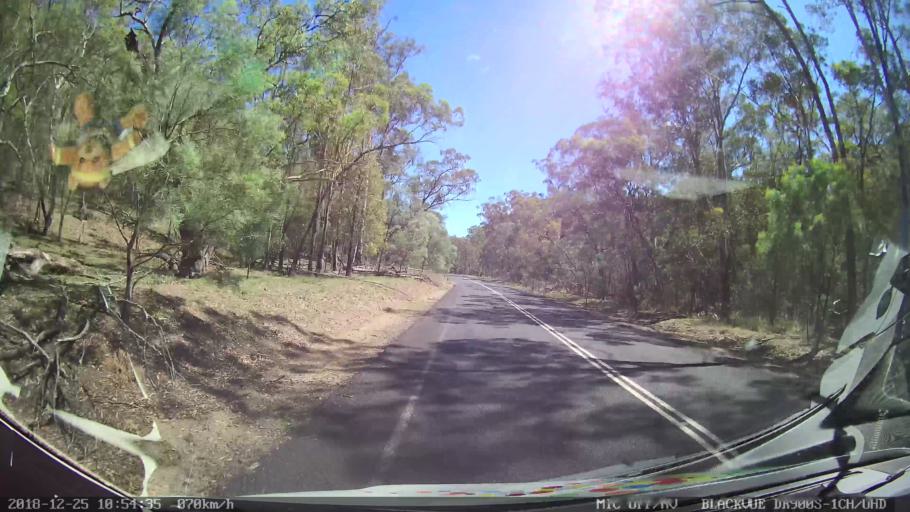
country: AU
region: New South Wales
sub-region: Upper Hunter Shire
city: Merriwa
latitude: -32.4082
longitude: 150.2735
